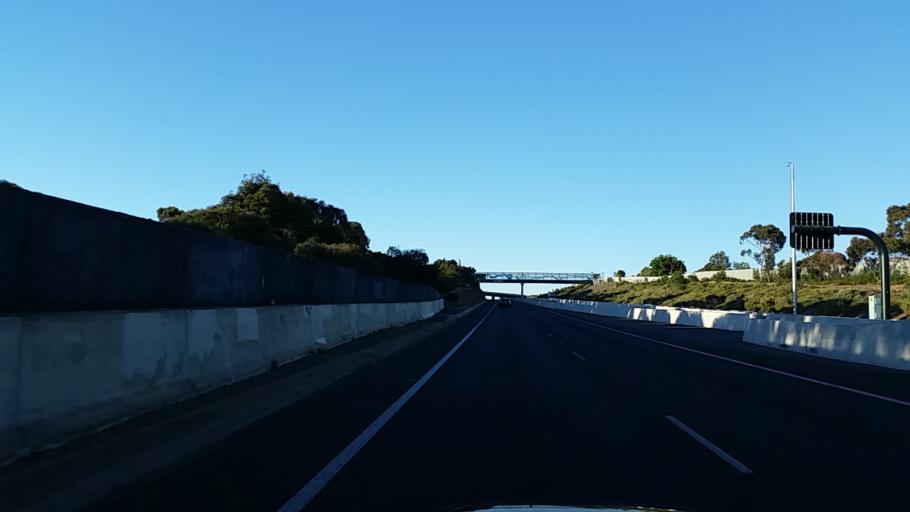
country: AU
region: South Australia
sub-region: Onkaparinga
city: Morphett Vale
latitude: -35.1217
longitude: 138.5078
